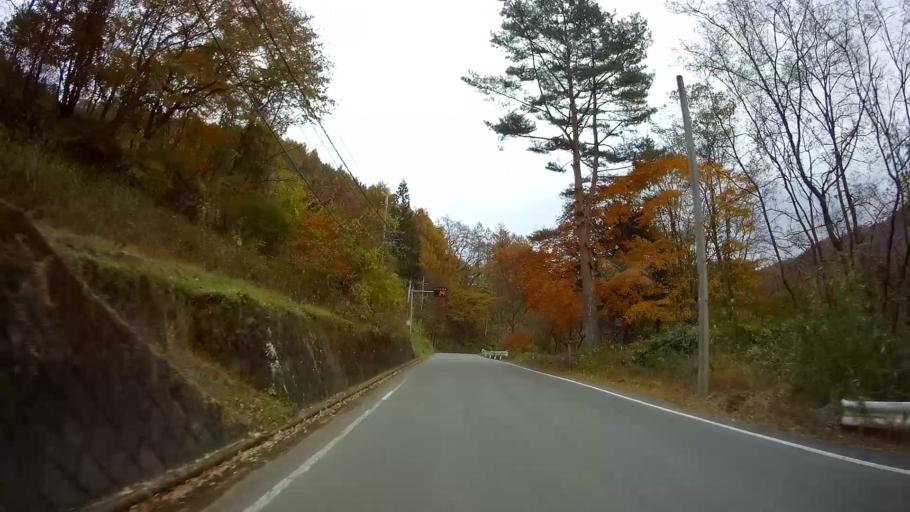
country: JP
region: Gunma
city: Nakanojomachi
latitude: 36.6400
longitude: 138.6518
